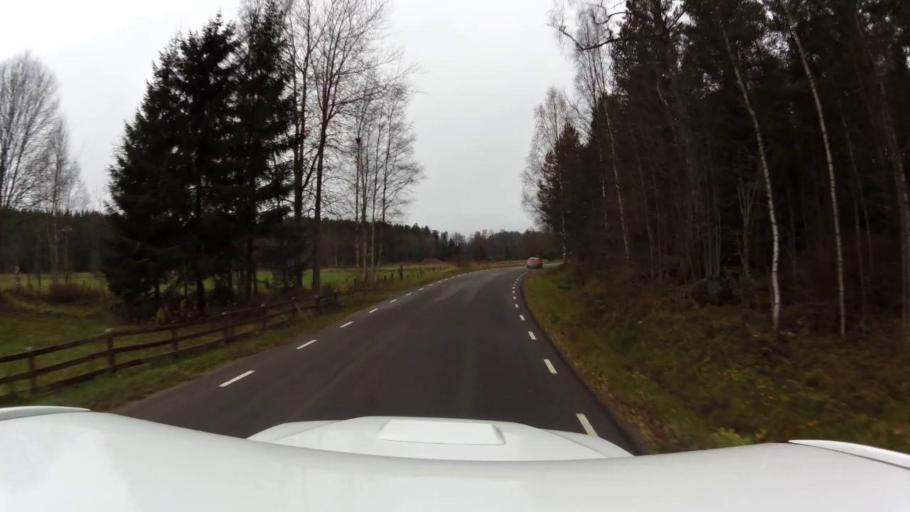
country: SE
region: OEstergoetland
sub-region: Kinda Kommun
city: Kisa
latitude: 58.1176
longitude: 15.4243
